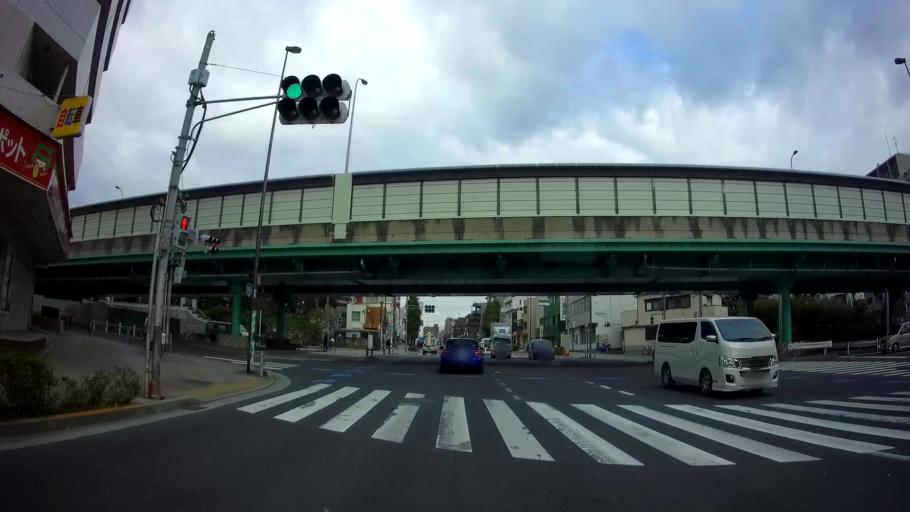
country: JP
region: Saitama
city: Kawaguchi
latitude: 35.7549
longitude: 139.6885
